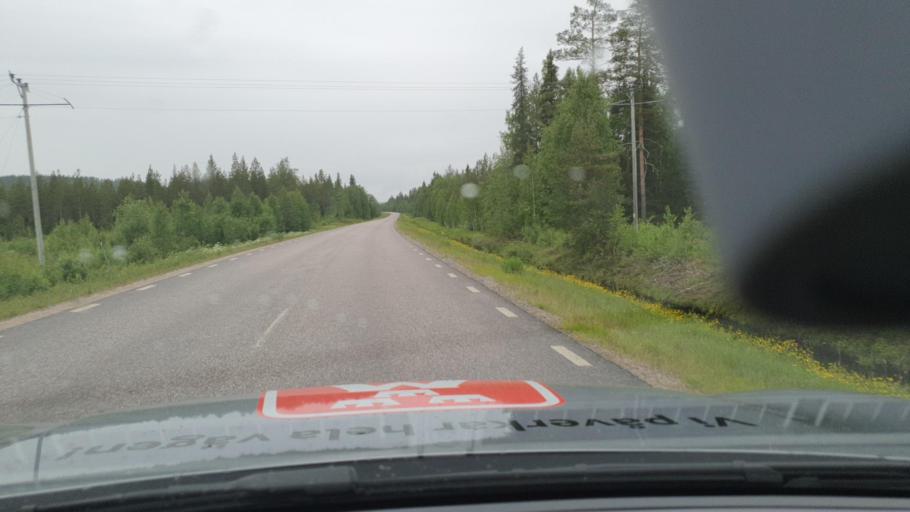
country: SE
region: Norrbotten
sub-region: Overtornea Kommun
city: OEvertornea
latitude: 66.3995
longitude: 23.5040
